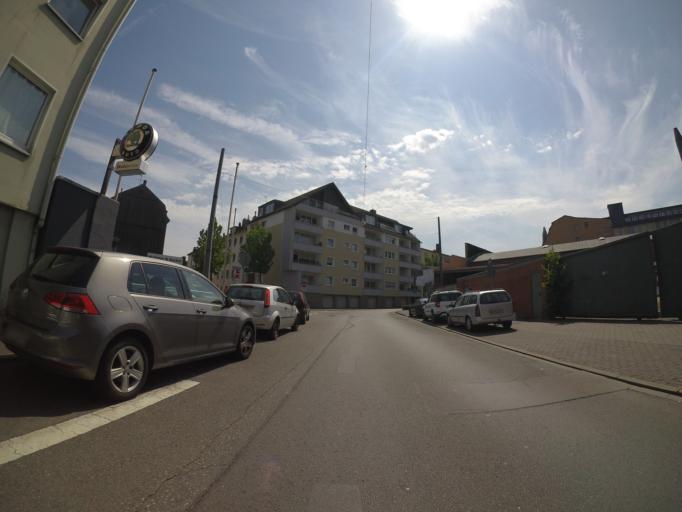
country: DE
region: North Rhine-Westphalia
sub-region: Regierungsbezirk Dusseldorf
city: Wuppertal
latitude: 51.2699
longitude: 7.2304
